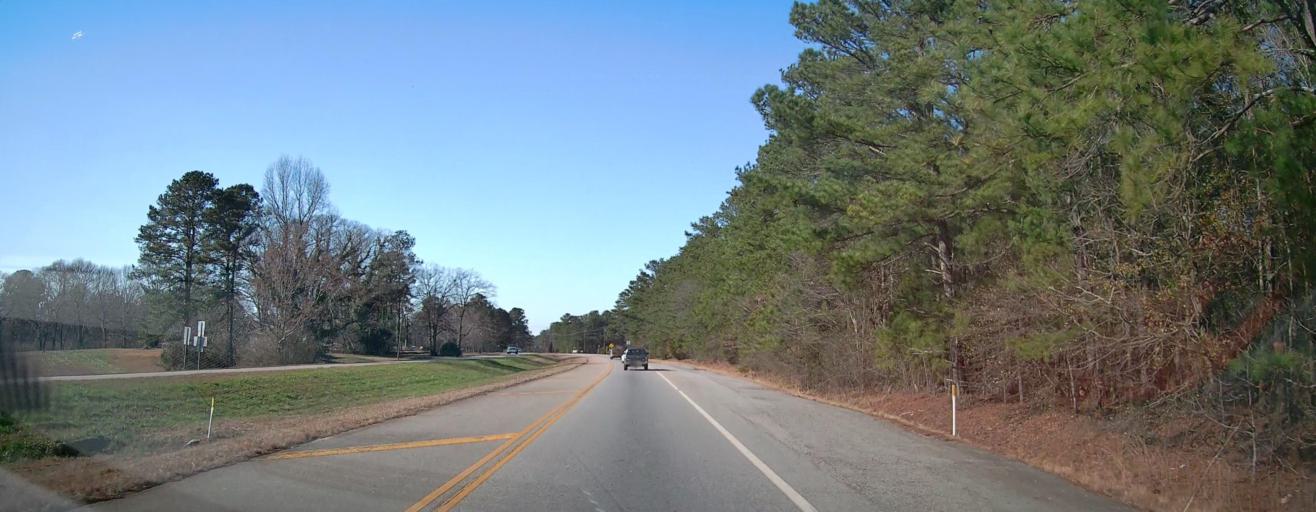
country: US
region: Georgia
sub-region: Butts County
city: Indian Springs
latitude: 33.2656
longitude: -83.9097
